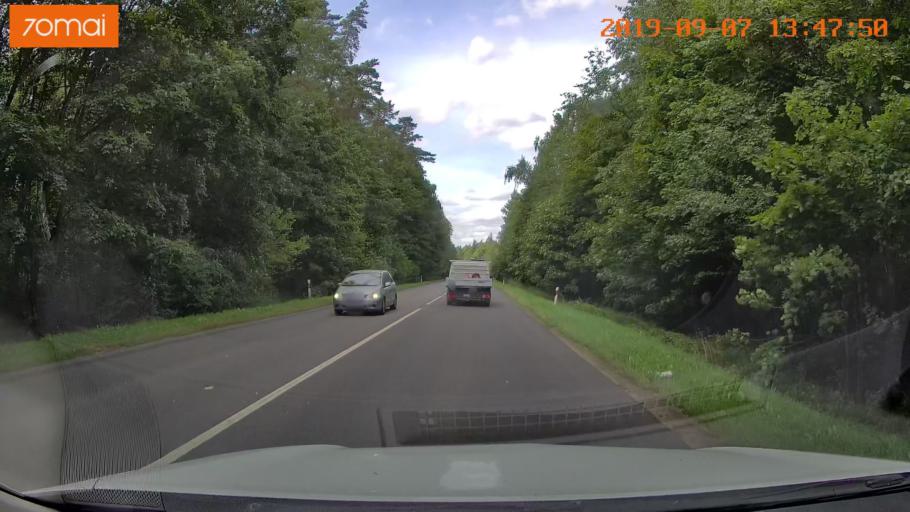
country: LT
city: Baltoji Voke
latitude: 54.5994
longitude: 25.2095
